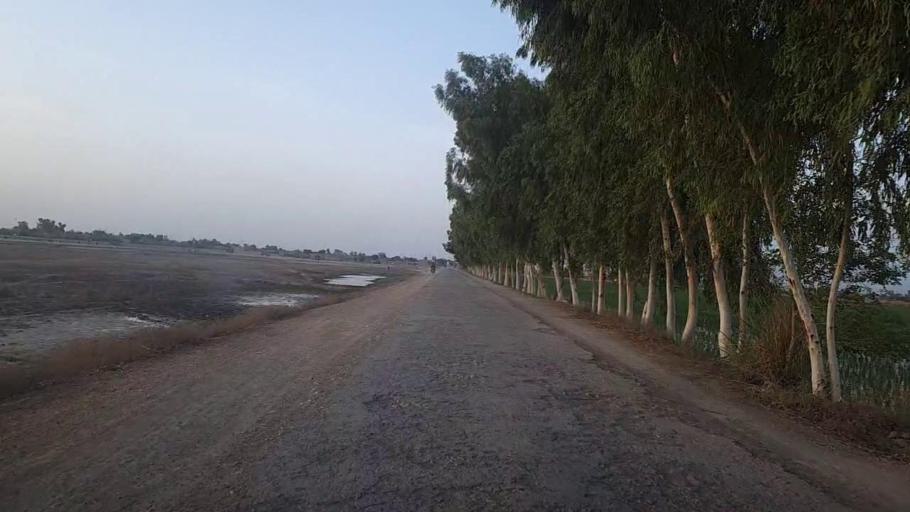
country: PK
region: Sindh
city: Radhan
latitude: 27.1280
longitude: 67.9292
